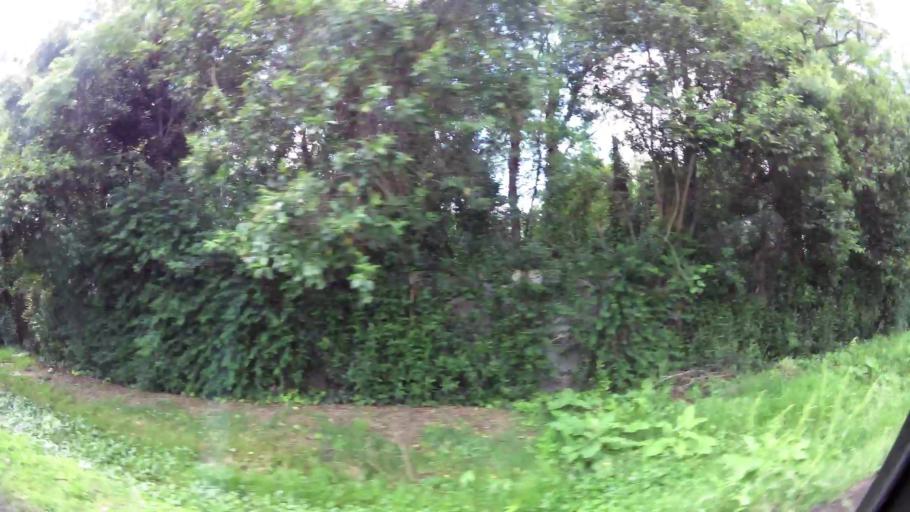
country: AR
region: Buenos Aires
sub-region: Partido de Quilmes
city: Quilmes
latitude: -34.8310
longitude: -58.2242
